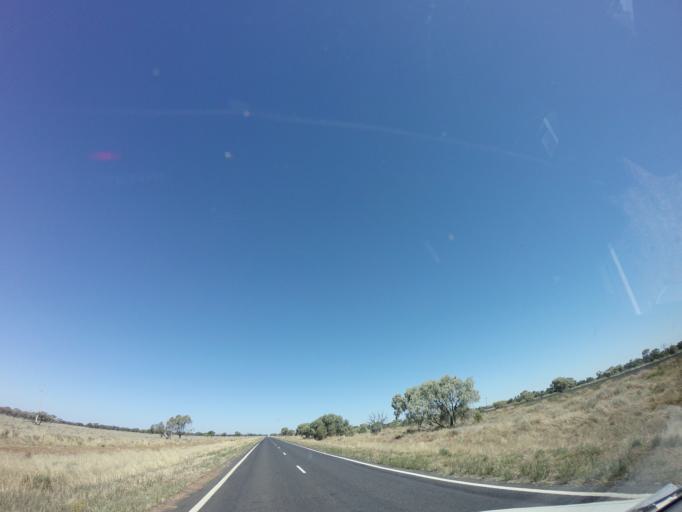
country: AU
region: New South Wales
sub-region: Bogan
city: Nyngan
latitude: -31.6199
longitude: 147.3058
